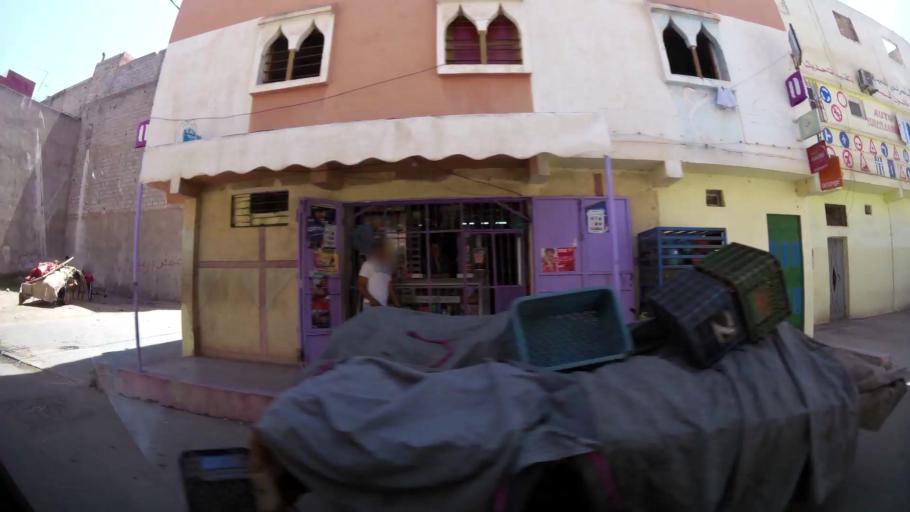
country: MA
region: Souss-Massa-Draa
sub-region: Inezgane-Ait Mellou
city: Inezgane
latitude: 30.3490
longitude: -9.4897
